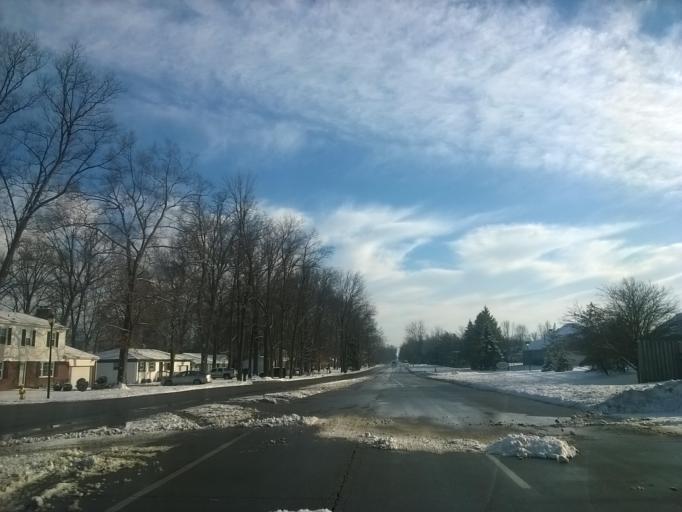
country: US
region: Indiana
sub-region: Hamilton County
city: Carmel
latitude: 39.9556
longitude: -86.1460
